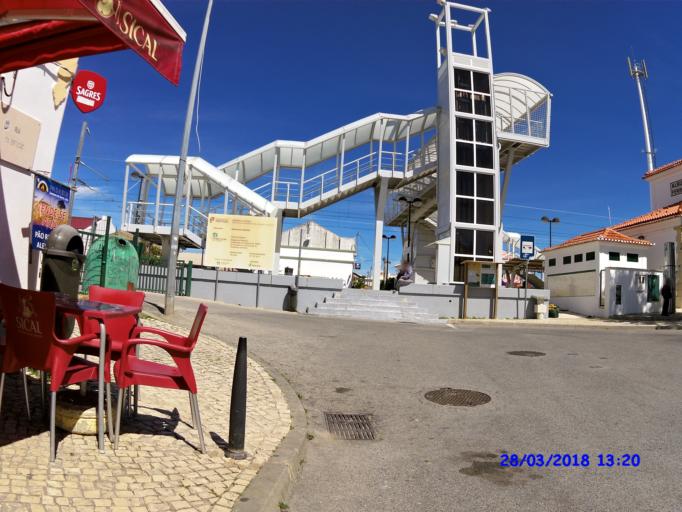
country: PT
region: Faro
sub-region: Albufeira
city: Ferreiras
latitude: 37.1285
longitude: -8.2335
